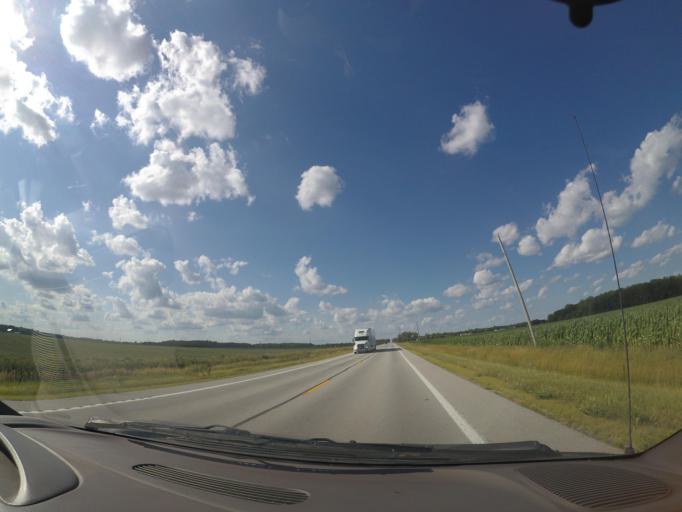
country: US
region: Ohio
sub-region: Wood County
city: Pemberville
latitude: 41.3959
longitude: -83.4161
